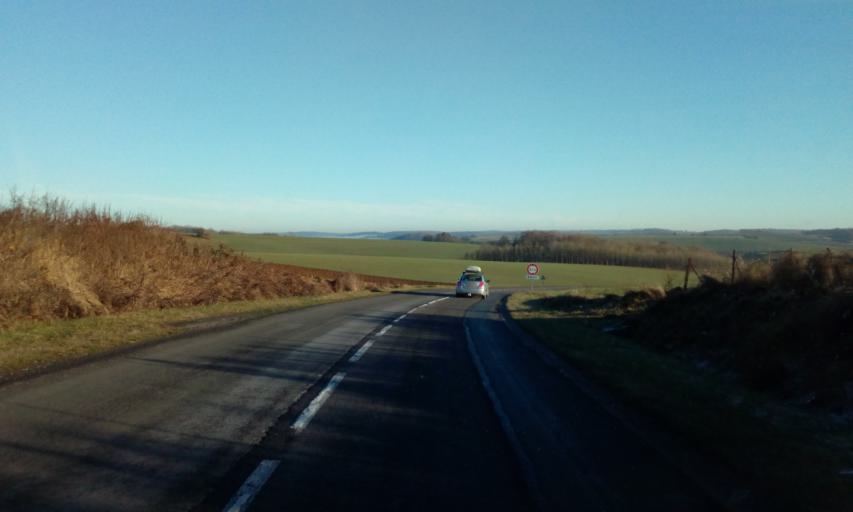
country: FR
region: Champagne-Ardenne
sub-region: Departement des Ardennes
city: Signy-le-Petit
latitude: 49.7815
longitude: 4.3719
